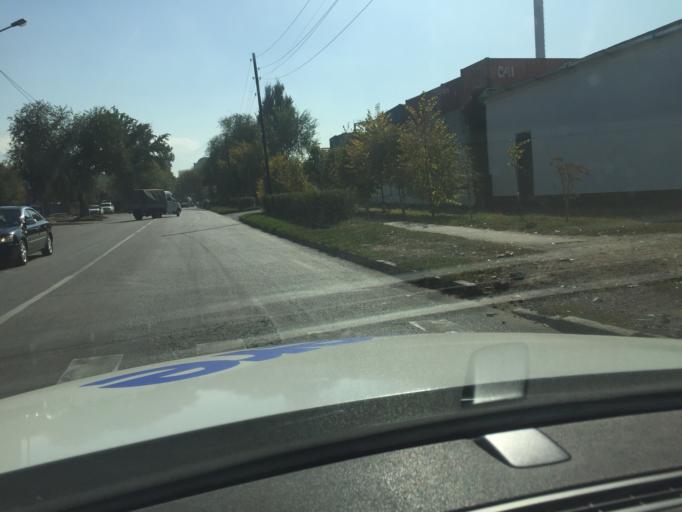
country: KZ
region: Almaty Qalasy
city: Almaty
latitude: 43.2615
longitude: 76.9108
